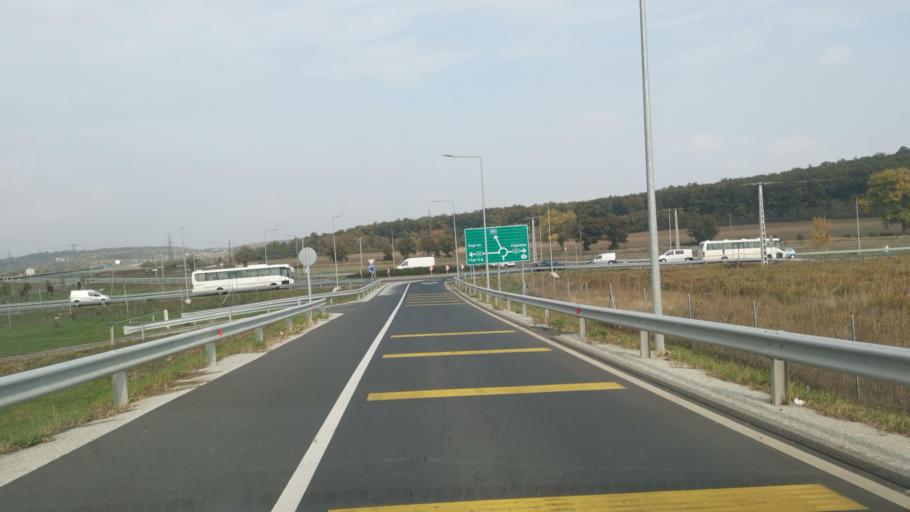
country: HU
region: Gyor-Moson-Sopron
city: Sopron
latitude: 47.6541
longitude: 16.6272
